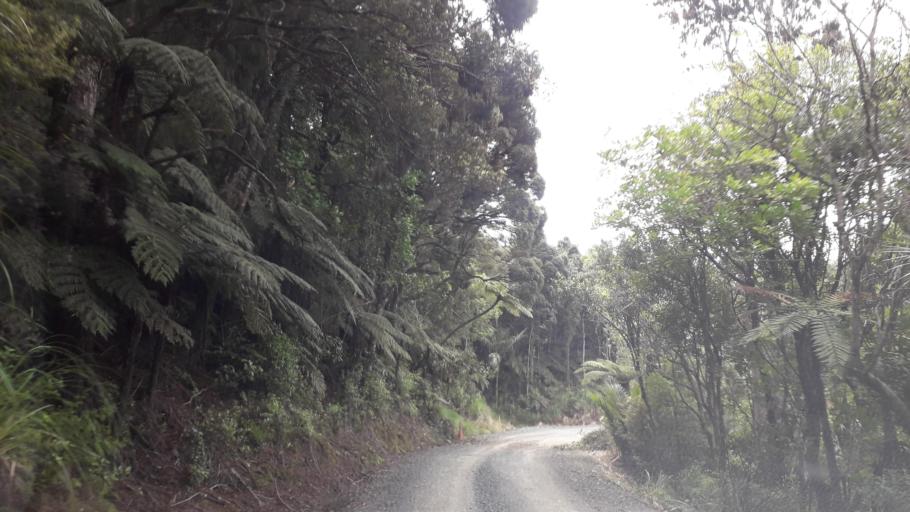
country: NZ
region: Northland
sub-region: Far North District
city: Kaitaia
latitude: -35.1976
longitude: 173.2830
